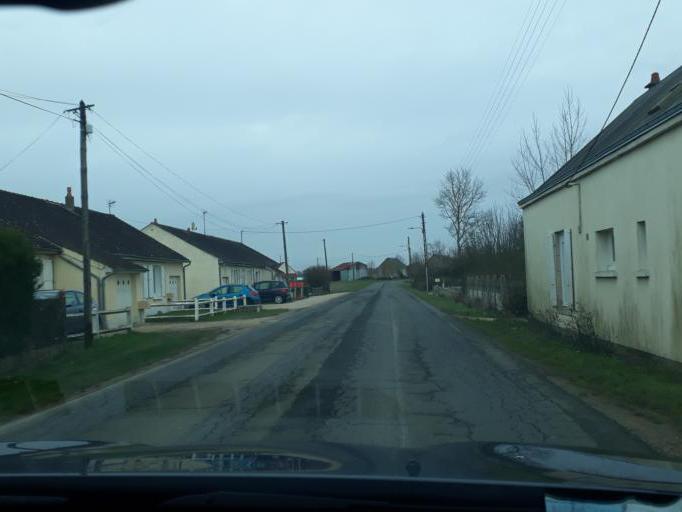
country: FR
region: Centre
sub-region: Departement du Loir-et-Cher
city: Oucques
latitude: 47.8248
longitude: 1.4005
